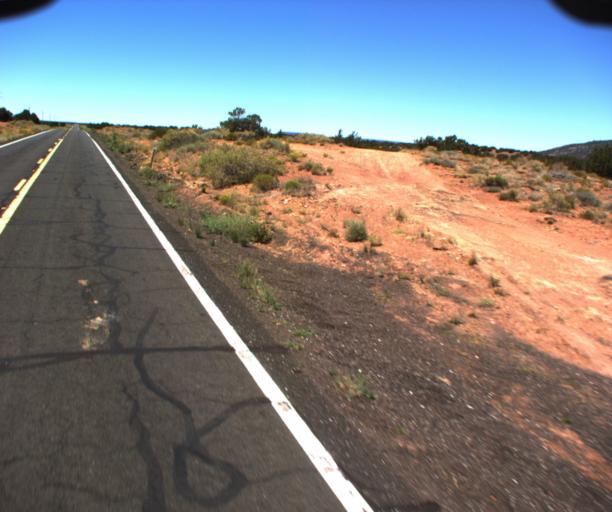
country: US
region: Arizona
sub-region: Coconino County
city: LeChee
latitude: 34.8589
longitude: -110.9175
